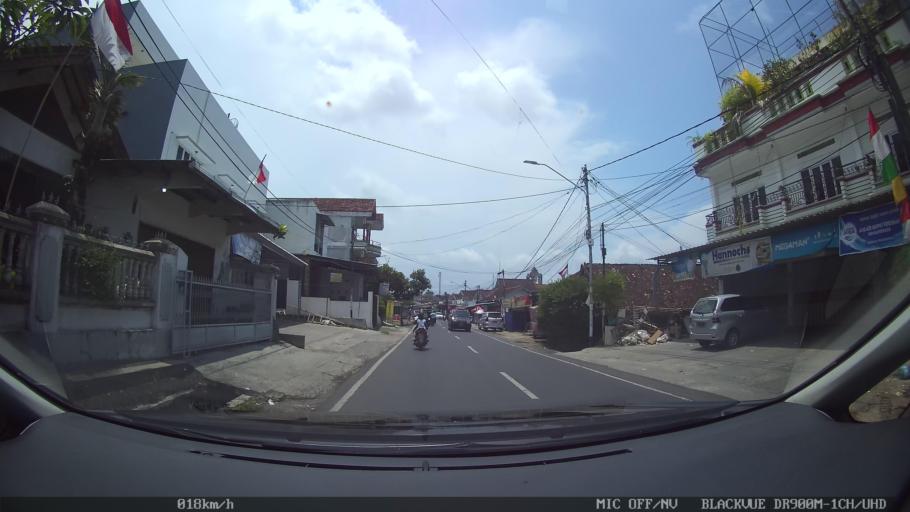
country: ID
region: Lampung
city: Kedaton
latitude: -5.4012
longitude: 105.2478
